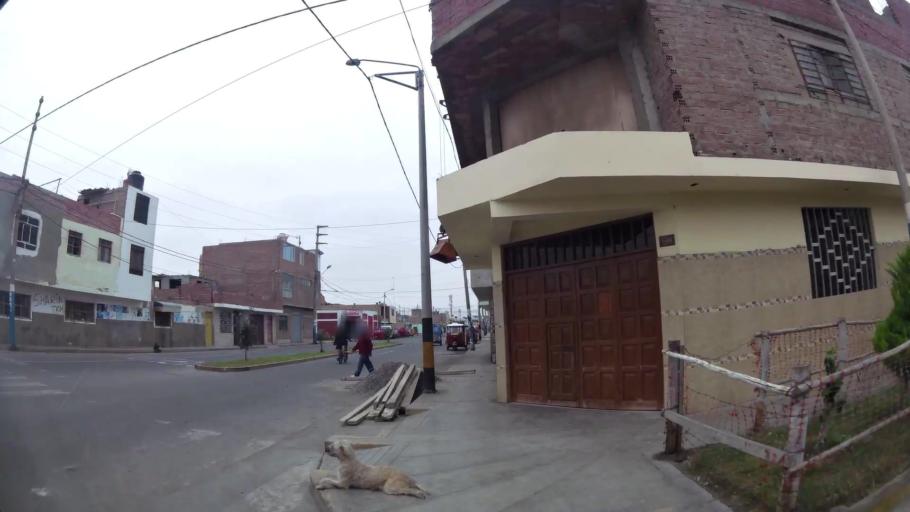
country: PE
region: Ica
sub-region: Provincia de Pisco
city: Pisco
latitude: -13.7146
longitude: -76.2080
